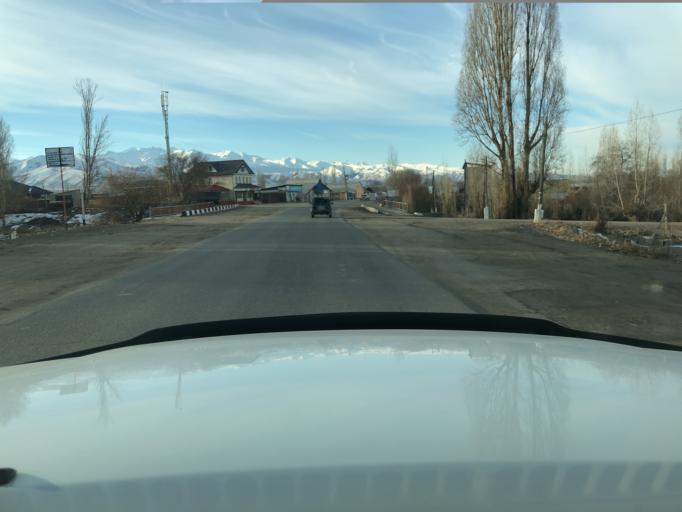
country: KG
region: Ysyk-Koel
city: Pokrovka
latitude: 42.3467
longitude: 78.0137
